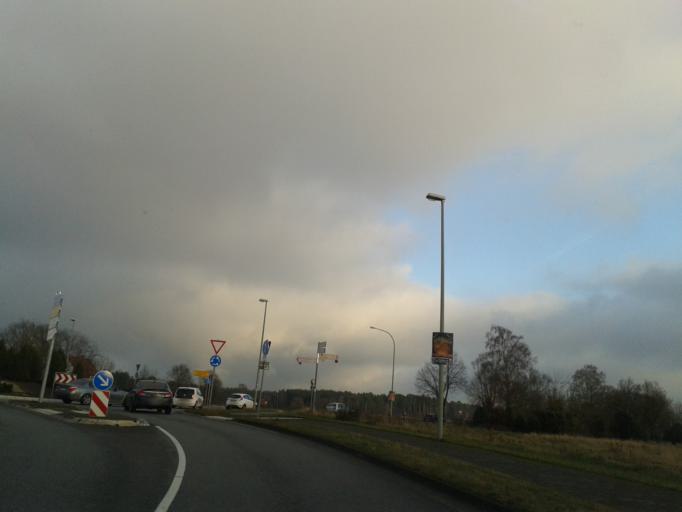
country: DE
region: North Rhine-Westphalia
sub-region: Regierungsbezirk Detmold
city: Augustdorf
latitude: 51.9069
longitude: 8.6837
